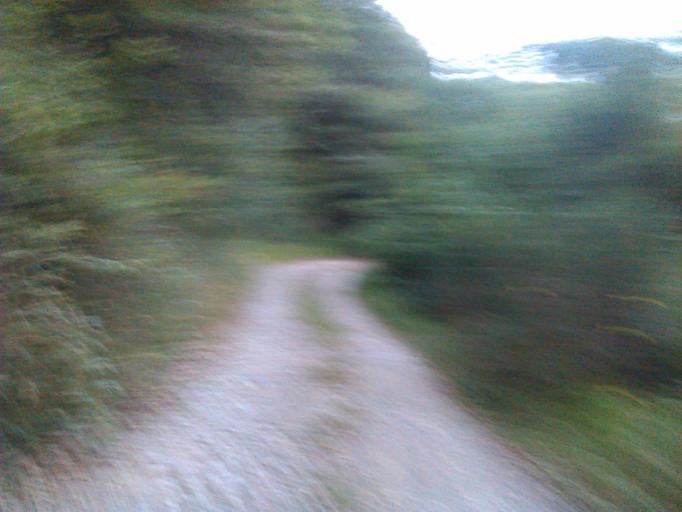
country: IT
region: Tuscany
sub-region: Province of Arezzo
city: Viciomaggio
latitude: 43.4487
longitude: 11.7571
